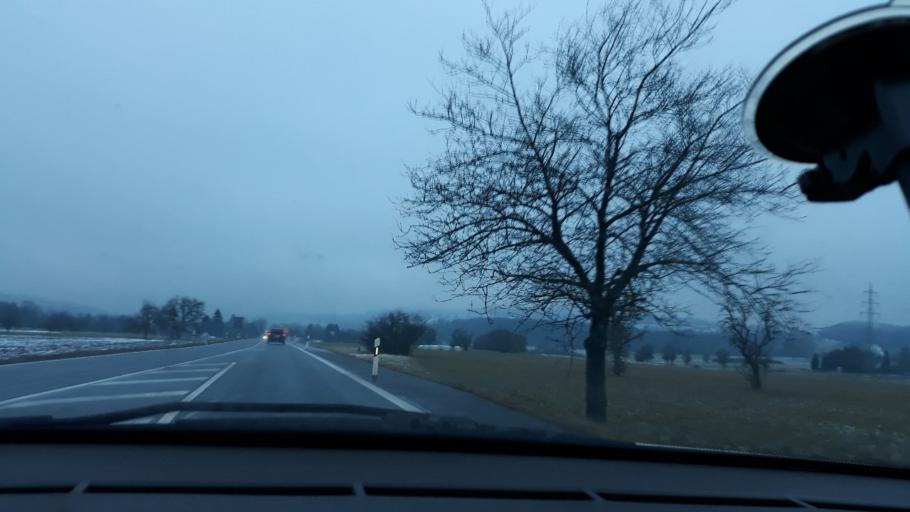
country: DE
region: Saarland
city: Gersheim
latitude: 49.2071
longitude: 7.1765
